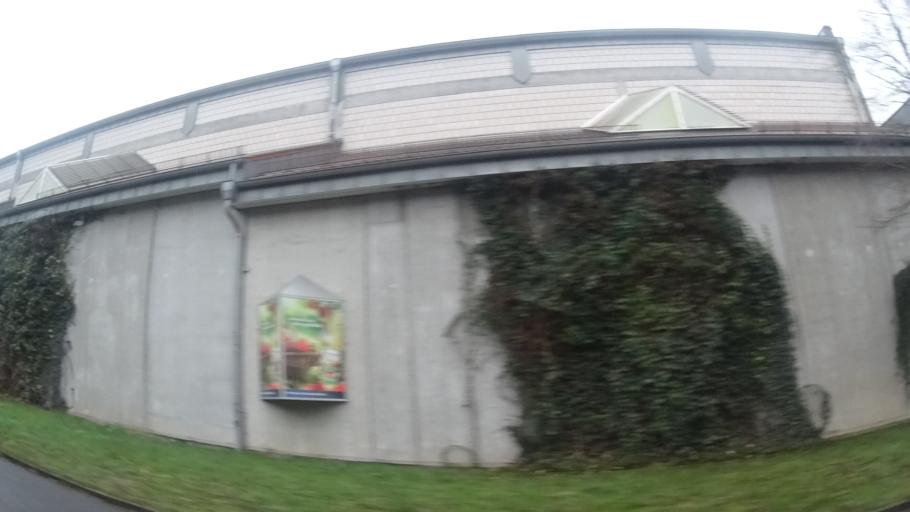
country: DE
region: Hesse
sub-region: Regierungsbezirk Kassel
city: Eichenzell
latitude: 50.4796
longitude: 9.7627
